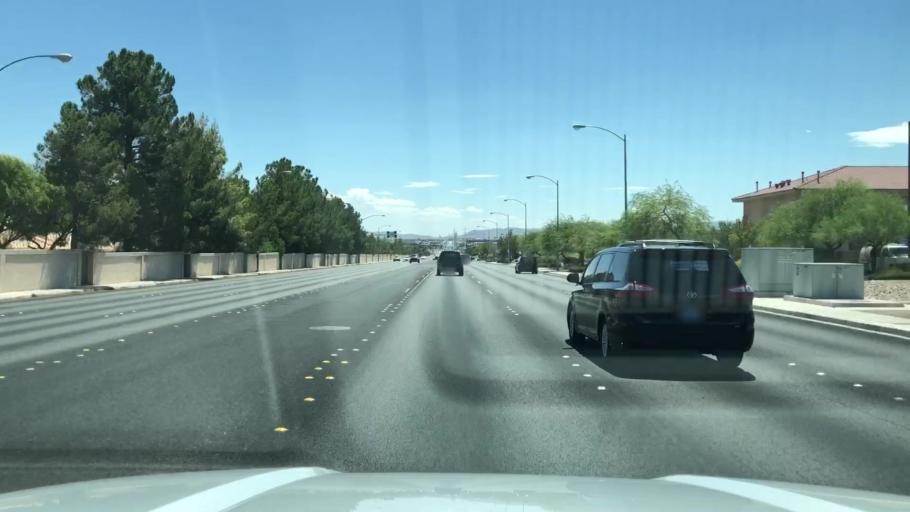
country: US
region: Nevada
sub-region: Clark County
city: Spring Valley
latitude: 36.0975
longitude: -115.2793
